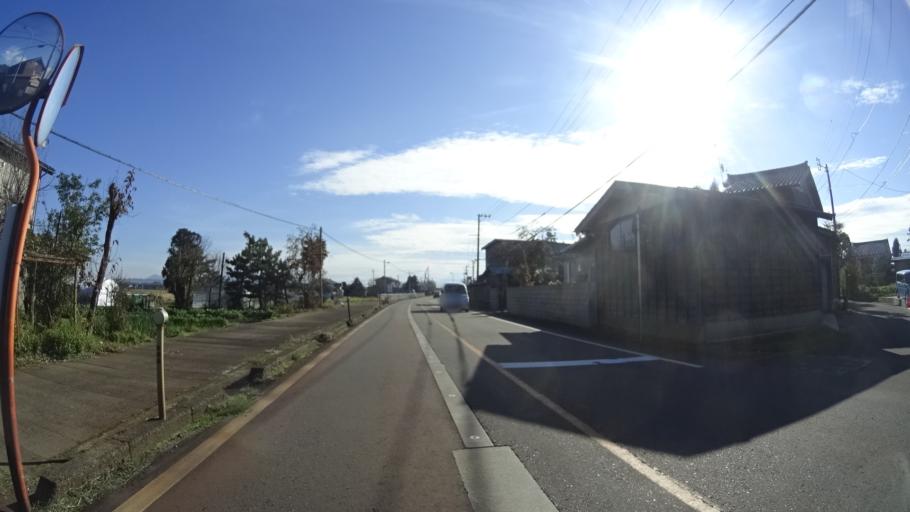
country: JP
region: Niigata
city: Mitsuke
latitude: 37.5517
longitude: 138.8664
